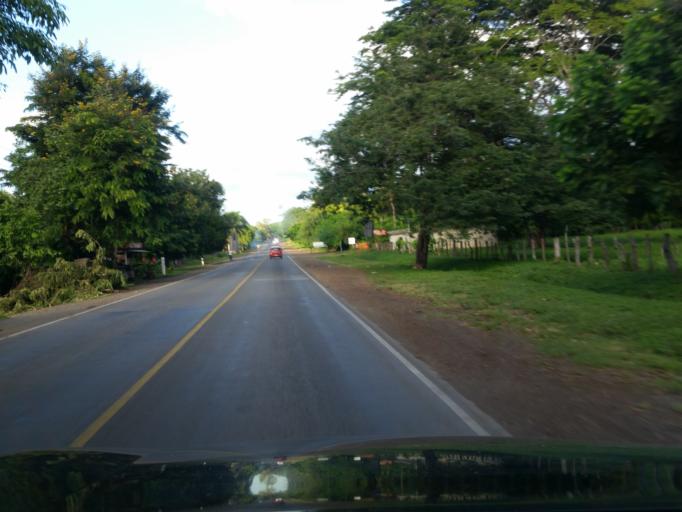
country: NI
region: Granada
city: Diriomo
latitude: 11.8291
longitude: -86.0370
